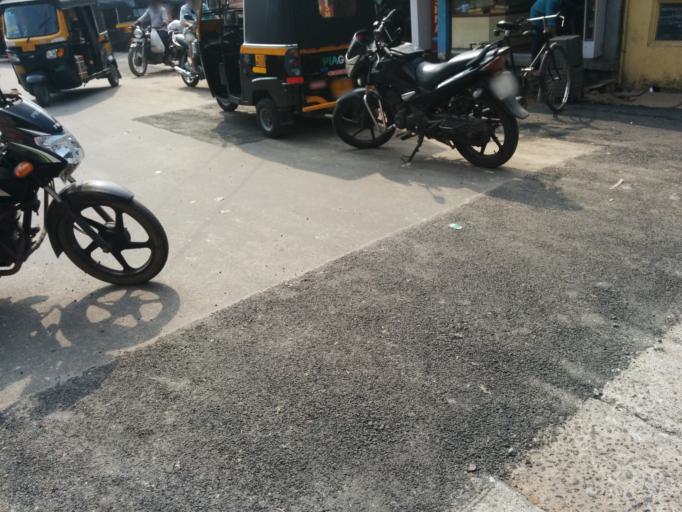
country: IN
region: Kerala
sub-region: Thiruvananthapuram
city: Thiruvananthapuram
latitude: 8.4820
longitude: 76.9541
